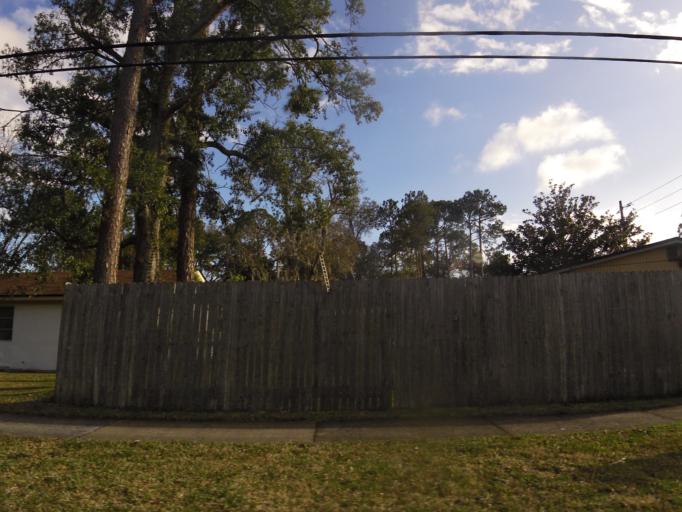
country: US
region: Florida
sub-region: Duval County
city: Jacksonville
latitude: 30.2758
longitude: -81.6096
